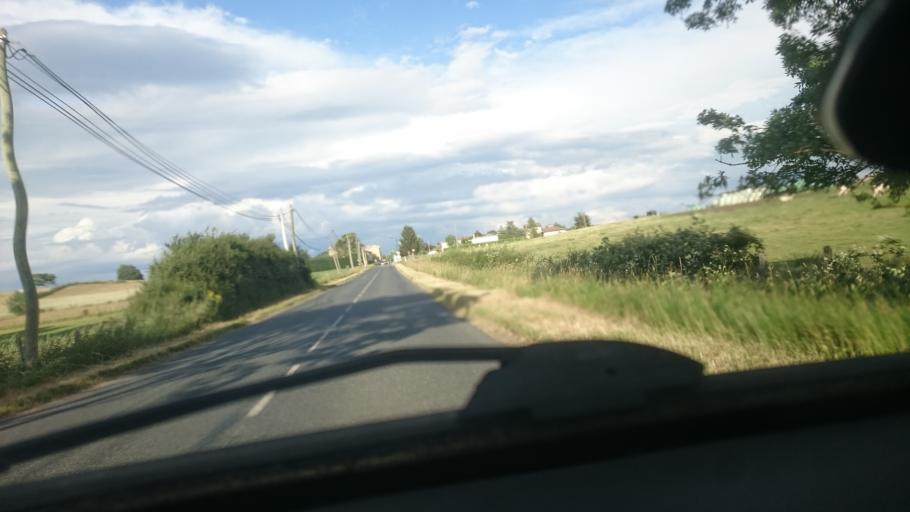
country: FR
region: Rhone-Alpes
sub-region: Departement du Rhone
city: Saint-Romain-de-Popey
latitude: 45.8787
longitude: 4.5486
